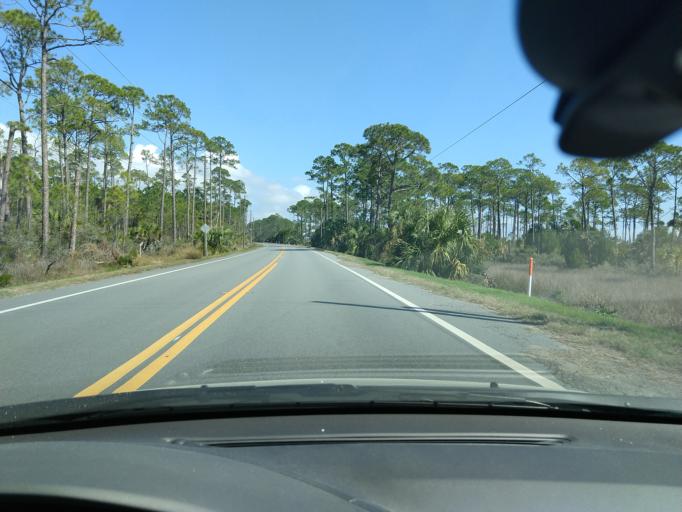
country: US
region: Florida
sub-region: Gulf County
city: Port Saint Joe
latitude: 29.6887
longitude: -85.2565
